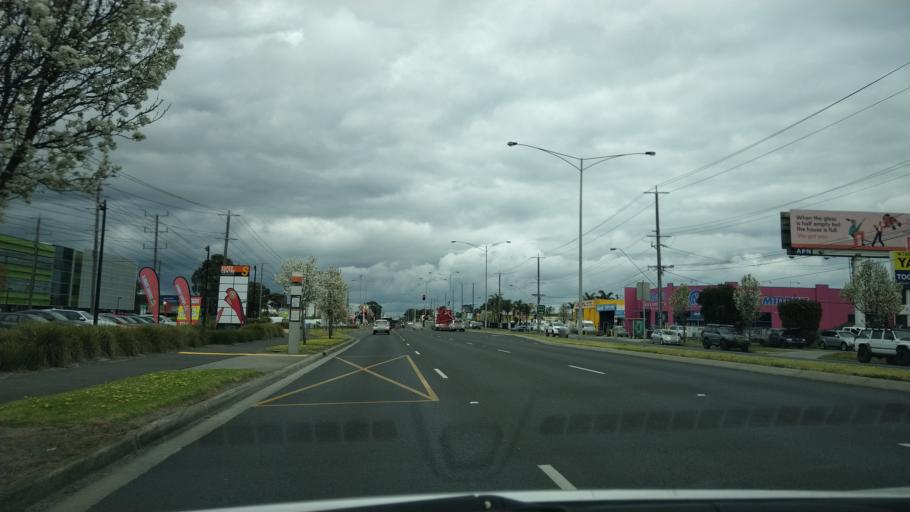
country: AU
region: Victoria
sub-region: Monash
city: Oakleigh South
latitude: -37.9484
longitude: 145.0779
